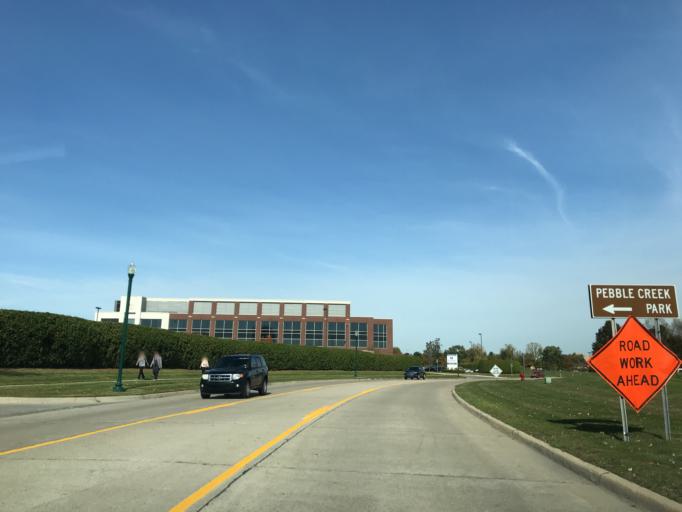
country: US
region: Michigan
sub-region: Oakland County
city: Franklin
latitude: 42.4894
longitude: -83.3038
